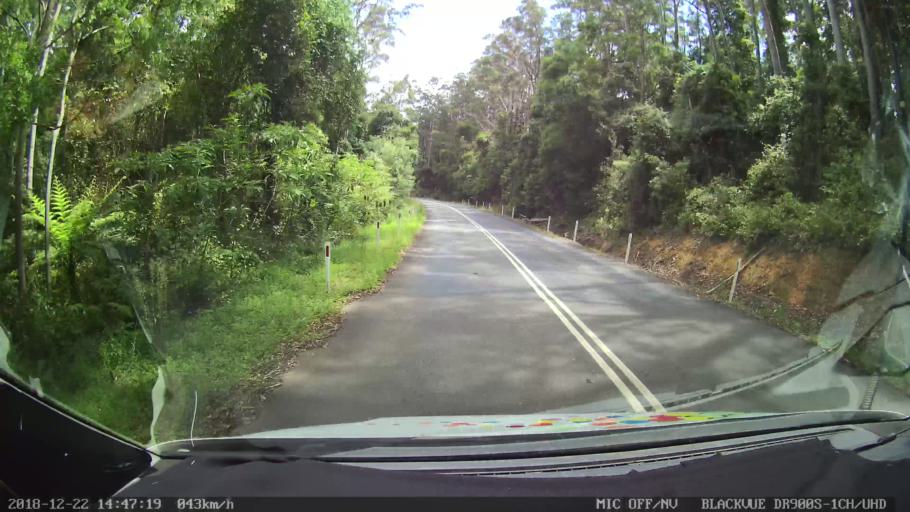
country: AU
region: New South Wales
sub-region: Bellingen
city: Dorrigo
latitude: -30.1751
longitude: 152.5569
